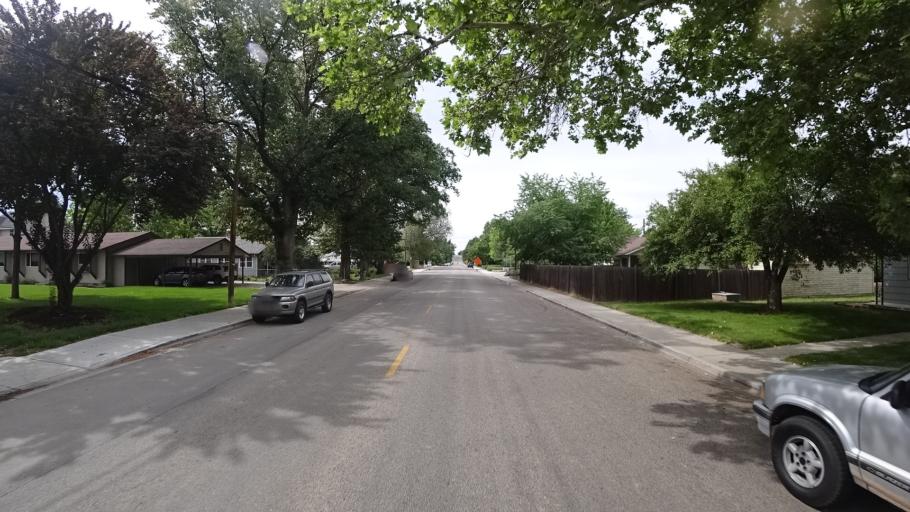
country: US
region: Idaho
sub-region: Ada County
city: Boise
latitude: 43.5844
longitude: -116.2237
